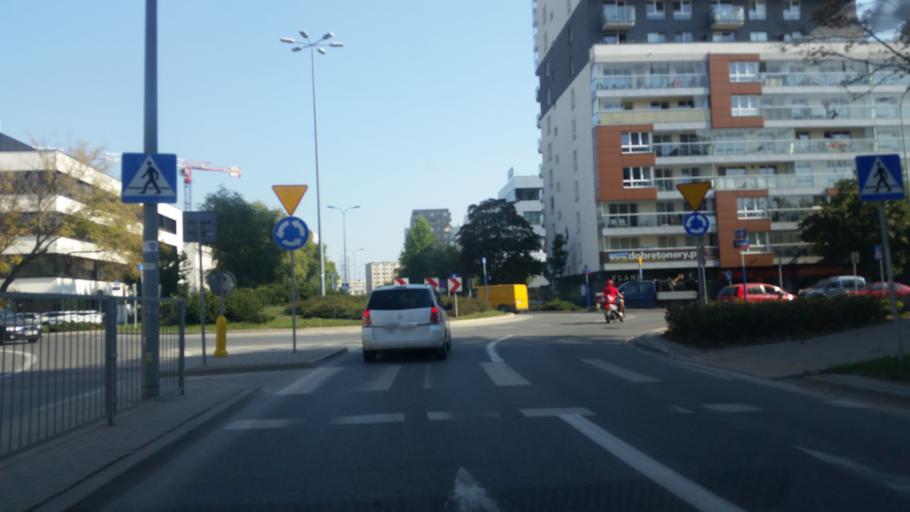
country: PL
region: Masovian Voivodeship
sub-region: Warszawa
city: Mokotow
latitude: 52.1763
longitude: 20.9947
